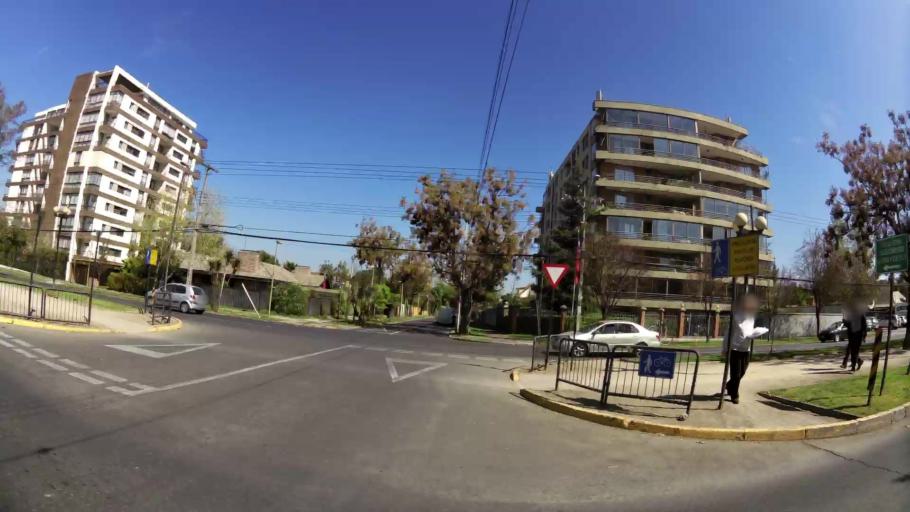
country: CL
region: Santiago Metropolitan
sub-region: Provincia de Santiago
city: Villa Presidente Frei, Nunoa, Santiago, Chile
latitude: -33.4229
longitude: -70.5642
